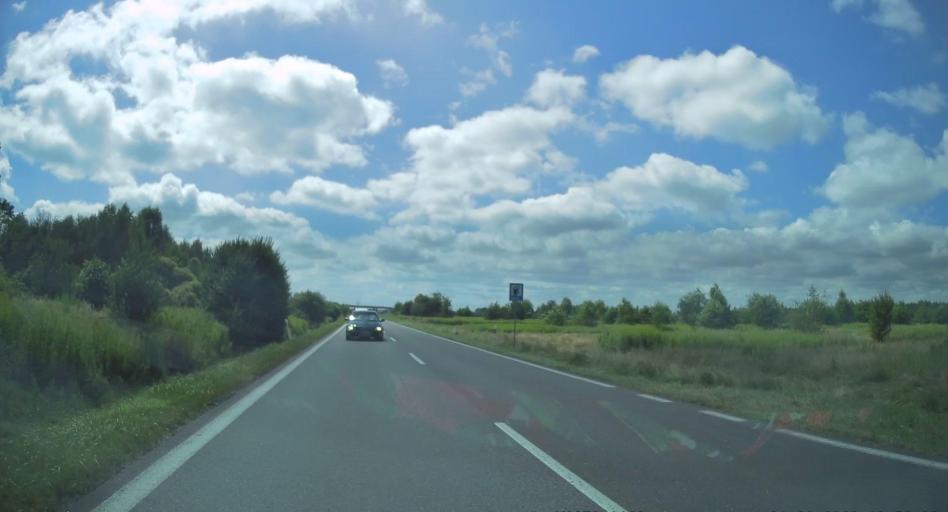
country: PL
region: Subcarpathian Voivodeship
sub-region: Powiat mielecki
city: Padew Narodowa
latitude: 50.3894
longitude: 21.4617
